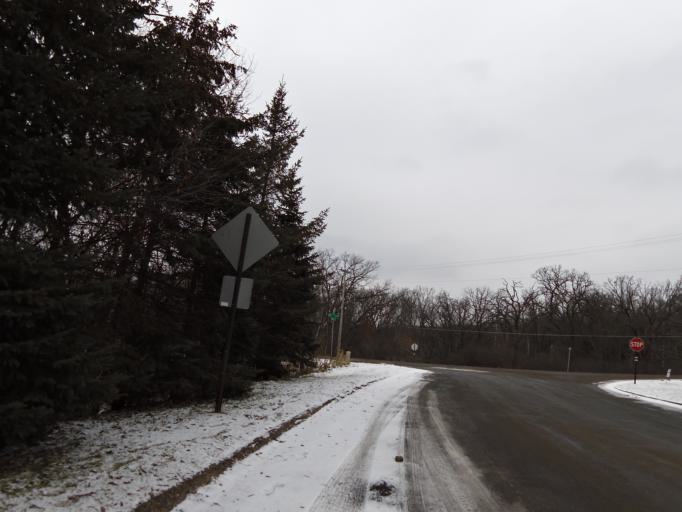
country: US
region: Minnesota
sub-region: Washington County
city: Lakeland
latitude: 44.9630
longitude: -92.8242
